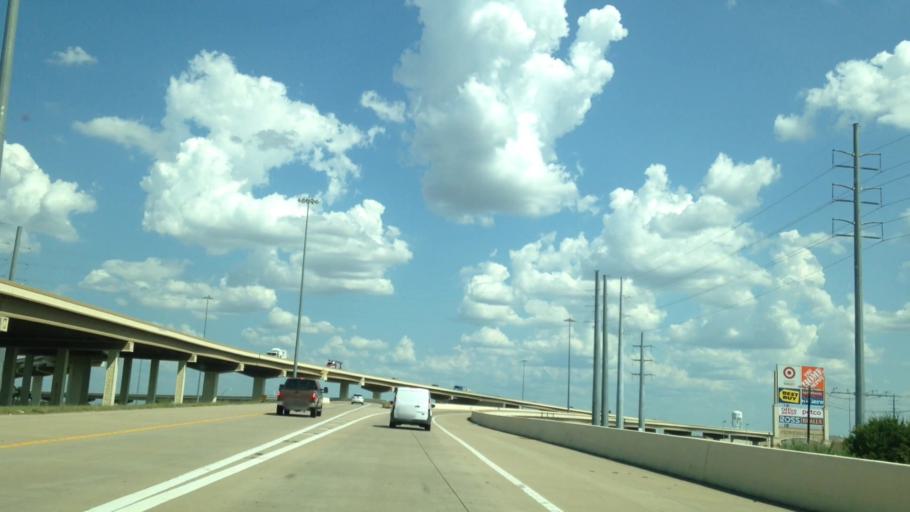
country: US
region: Texas
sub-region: Travis County
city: Pflugerville
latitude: 30.4757
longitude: -97.5970
